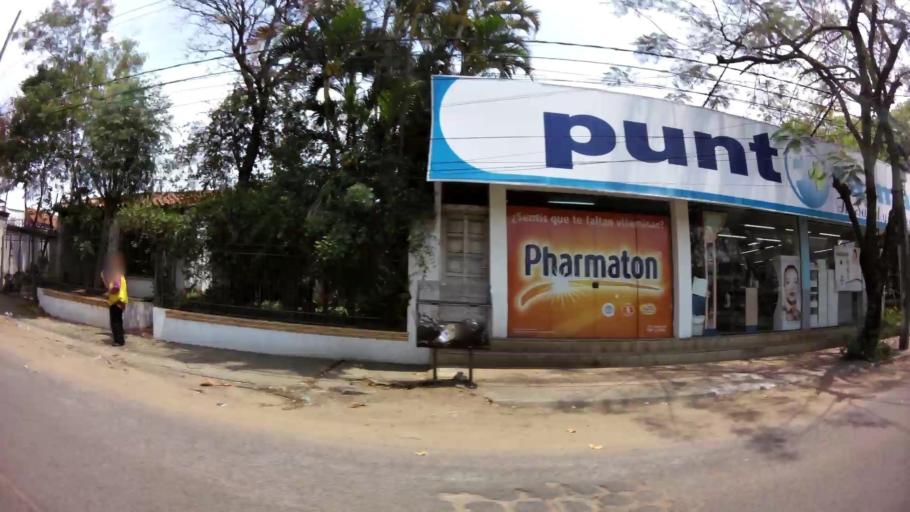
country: PY
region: Central
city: Fernando de la Mora
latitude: -25.3127
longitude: -57.5657
